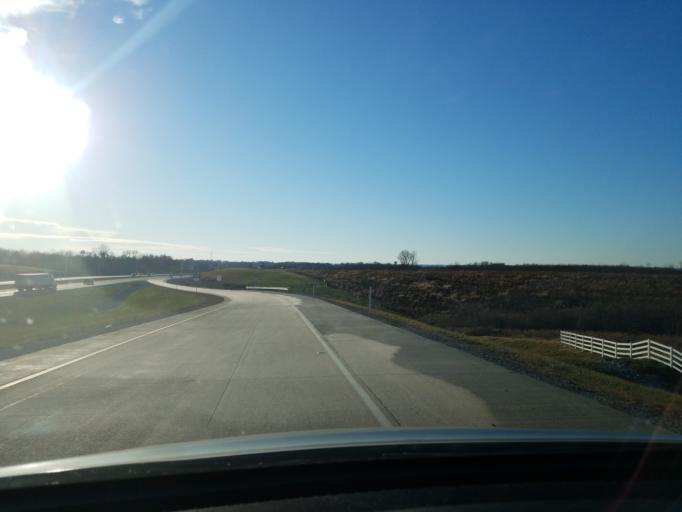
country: US
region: Indiana
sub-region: Clark County
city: Oak Park
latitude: 38.3497
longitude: -85.6682
